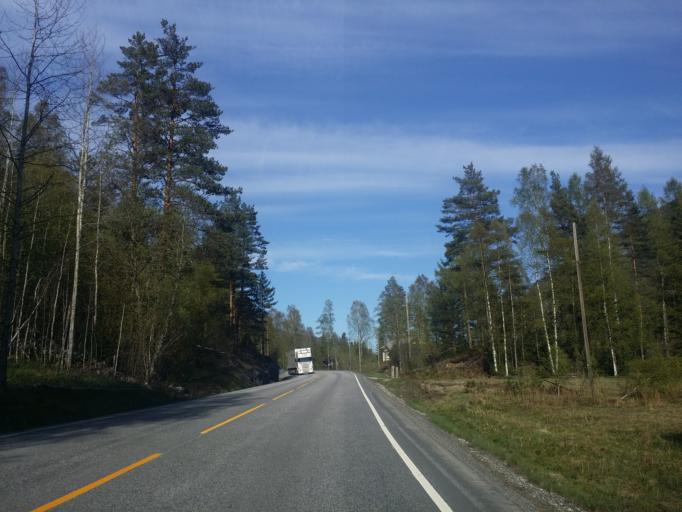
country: NO
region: Telemark
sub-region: Hjartdal
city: Sauland
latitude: 59.6117
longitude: 8.7846
